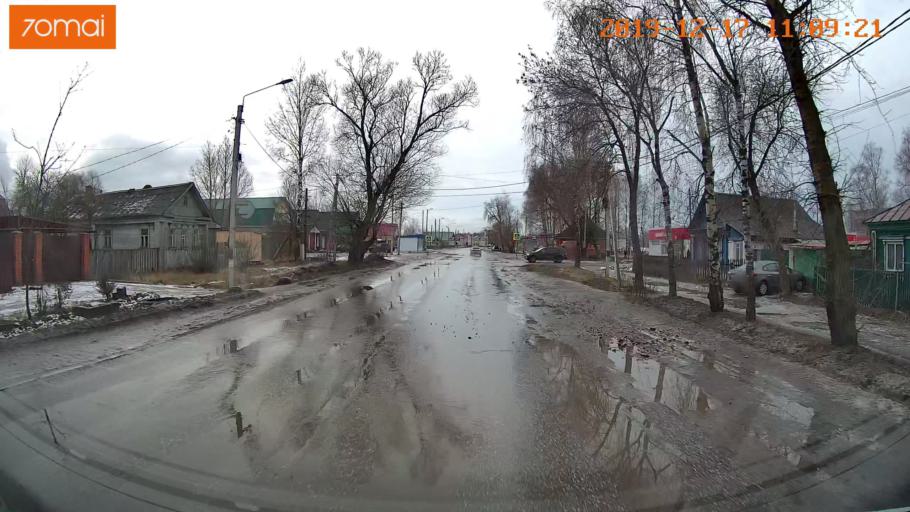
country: RU
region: Vladimir
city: Gus'-Khrustal'nyy
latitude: 55.6012
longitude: 40.6425
